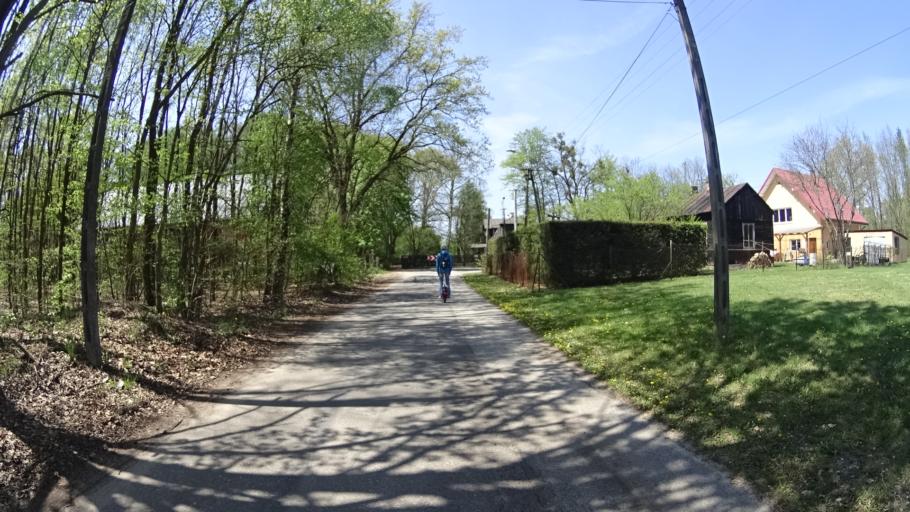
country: PL
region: Masovian Voivodeship
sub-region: Powiat warszawski zachodni
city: Truskaw
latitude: 52.2850
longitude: 20.7243
